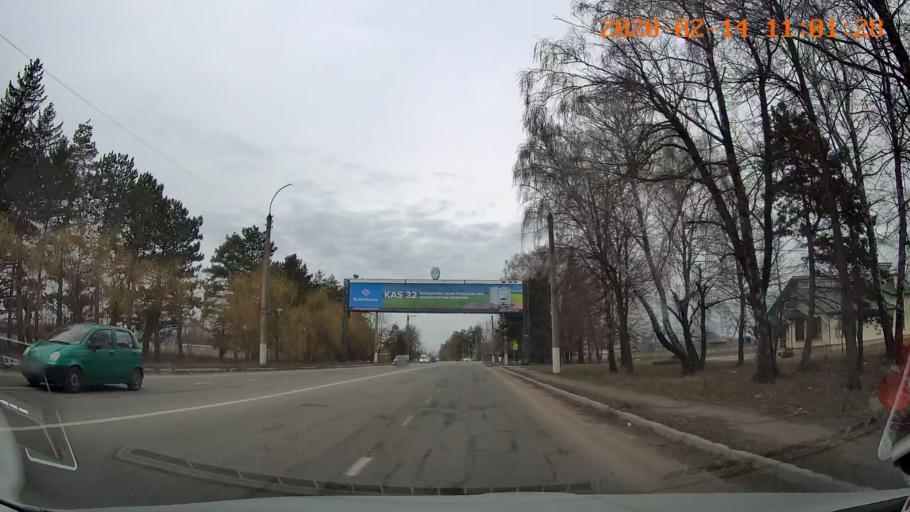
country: MD
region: Raionul Edinet
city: Edinet
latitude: 48.1599
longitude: 27.3288
